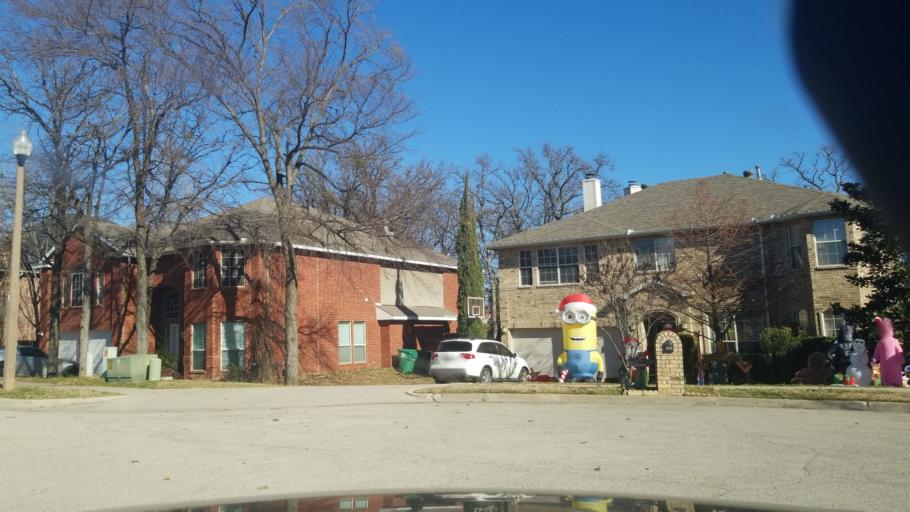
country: US
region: Texas
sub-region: Denton County
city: Corinth
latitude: 33.1478
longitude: -97.1140
